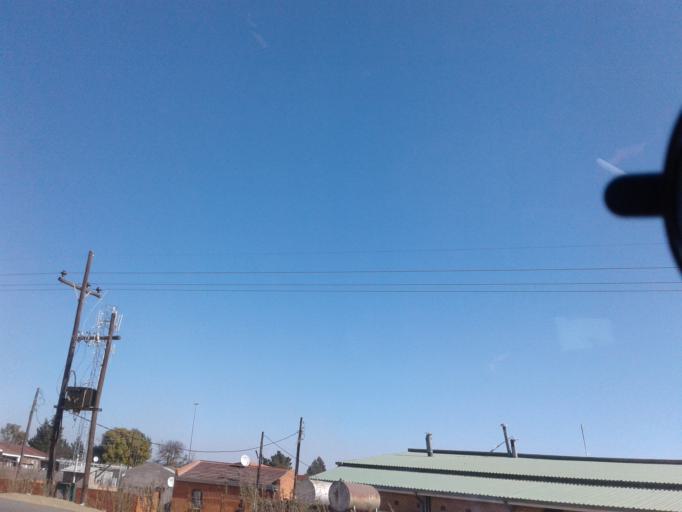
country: LS
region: Maseru
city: Maseru
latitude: -29.2933
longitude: 27.5180
